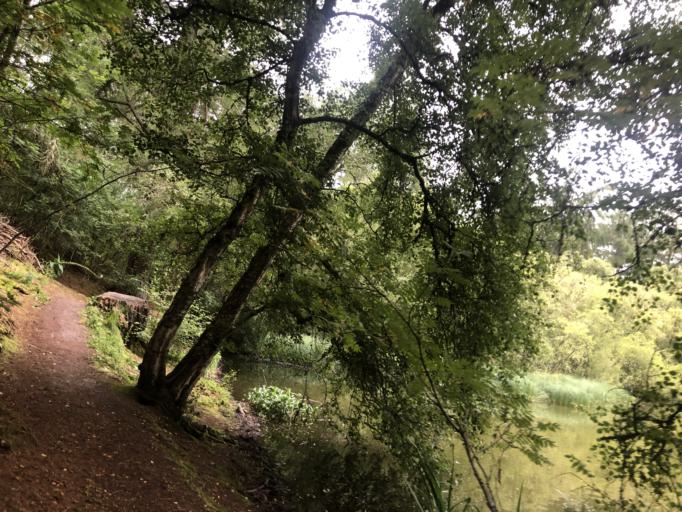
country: GB
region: Scotland
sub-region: Highland
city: Kingussie
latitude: 57.0663
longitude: -4.1130
